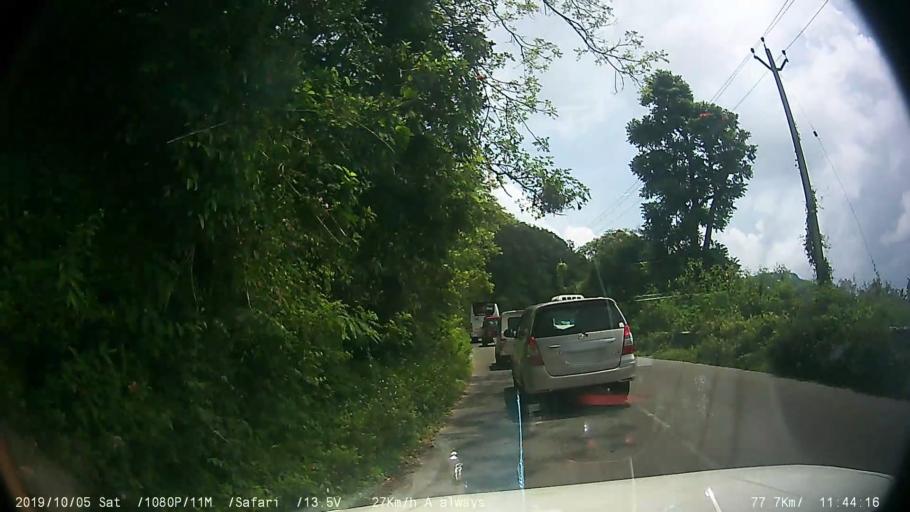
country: IN
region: Kerala
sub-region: Kottayam
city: Erattupetta
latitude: 9.5706
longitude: 77.0006
